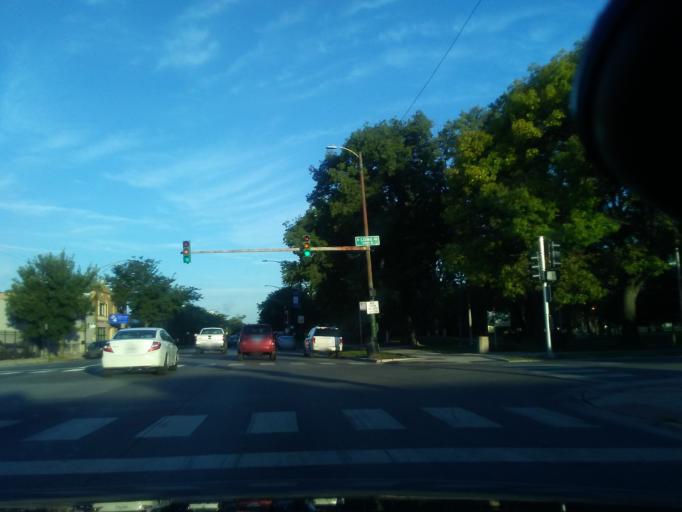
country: US
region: Illinois
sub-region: Cook County
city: Harwood Heights
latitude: 41.9533
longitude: -87.7619
